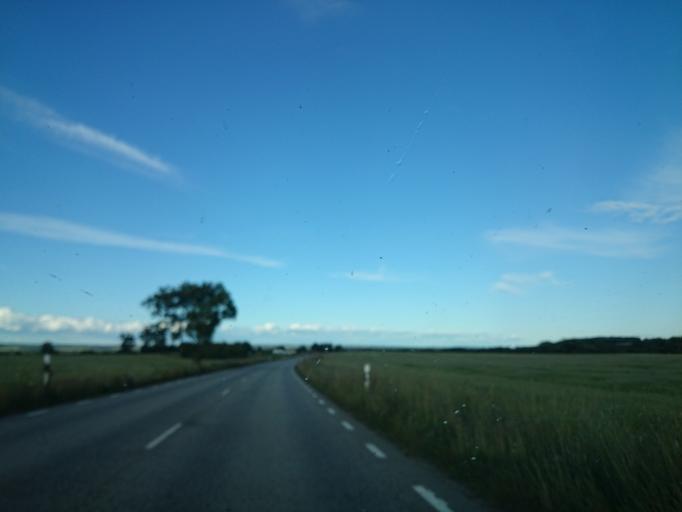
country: SE
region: Skane
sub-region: Eslovs Kommun
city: Eslov
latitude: 55.7177
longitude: 13.3207
